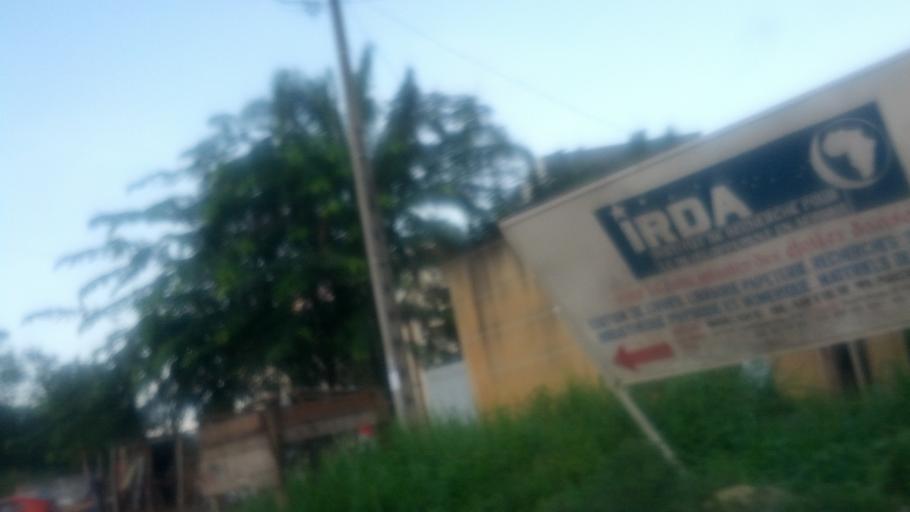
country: CI
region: Vallee du Bandama
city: Bouake
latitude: 7.6873
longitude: -5.0584
